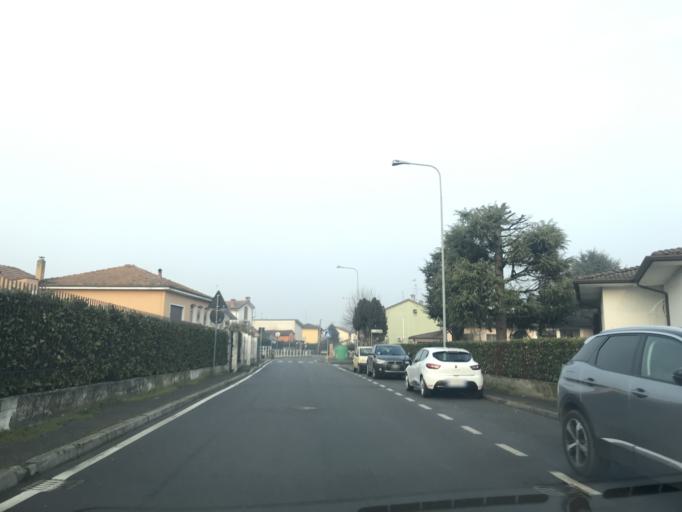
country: IT
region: Lombardy
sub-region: Provincia di Lodi
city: Villanova del Sillaro
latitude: 45.2381
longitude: 9.4815
